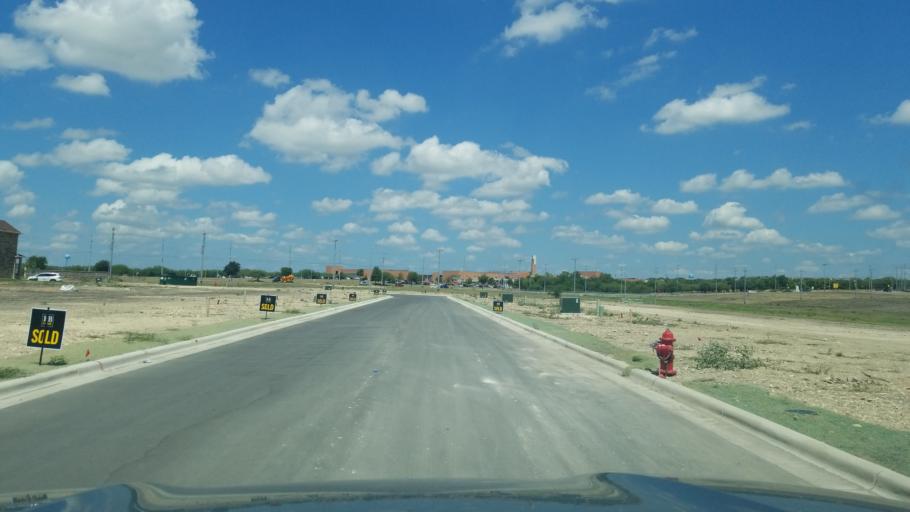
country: US
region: Texas
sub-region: Bexar County
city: Converse
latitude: 29.5400
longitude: -98.3205
